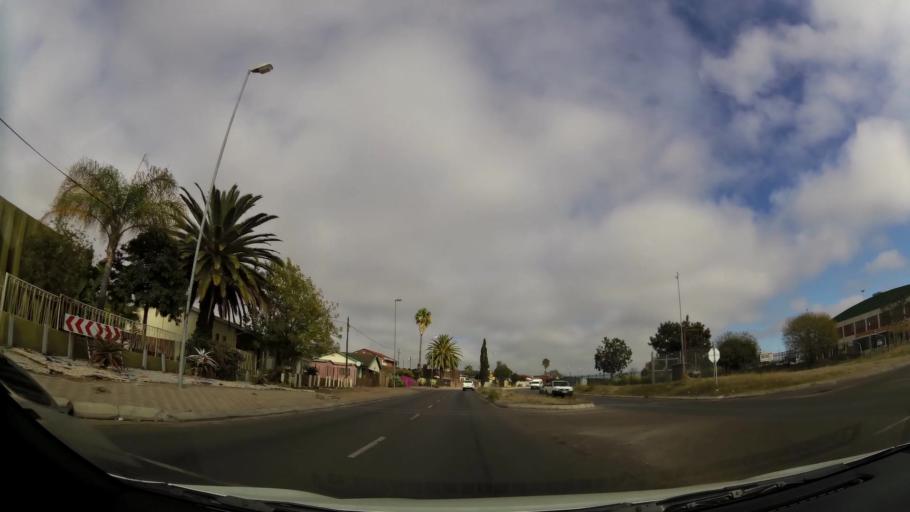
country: ZA
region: Limpopo
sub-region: Capricorn District Municipality
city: Polokwane
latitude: -23.8548
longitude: 29.3854
